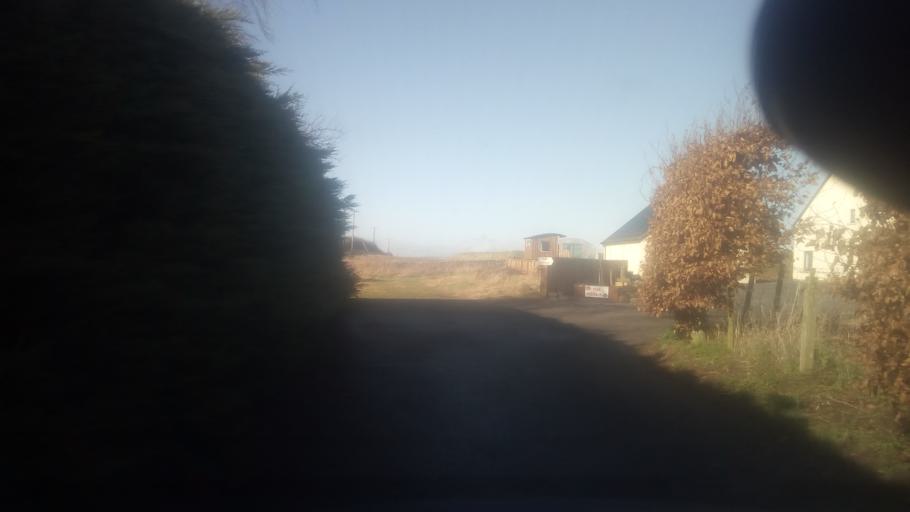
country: GB
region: Scotland
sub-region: The Scottish Borders
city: Jedburgh
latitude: 55.4897
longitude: -2.5280
